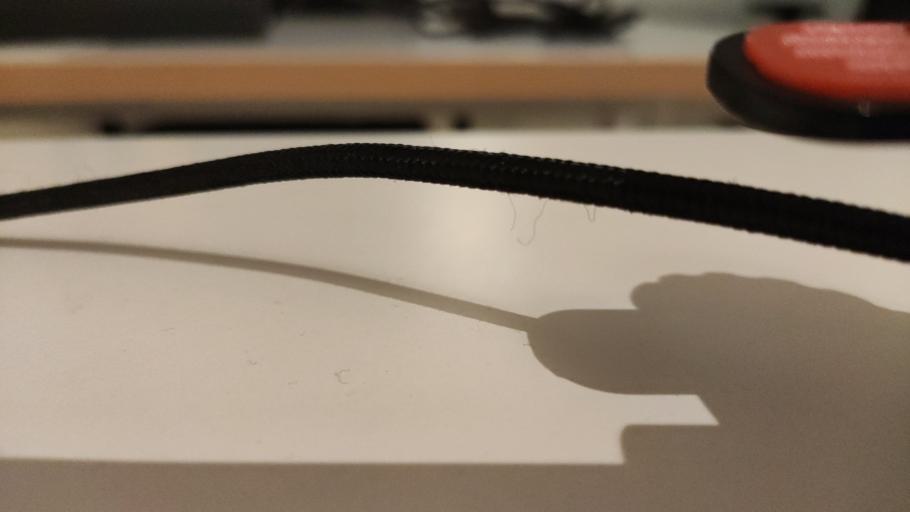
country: RU
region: Moskovskaya
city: Kurovskoye
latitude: 55.6006
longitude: 38.9256
